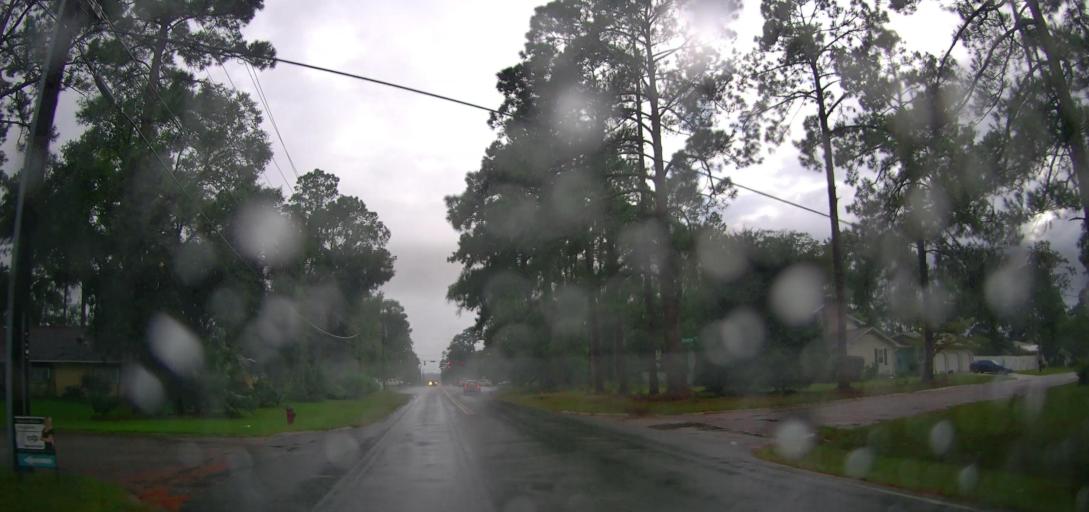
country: US
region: Georgia
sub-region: Ware County
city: Waycross
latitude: 31.2153
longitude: -82.3293
